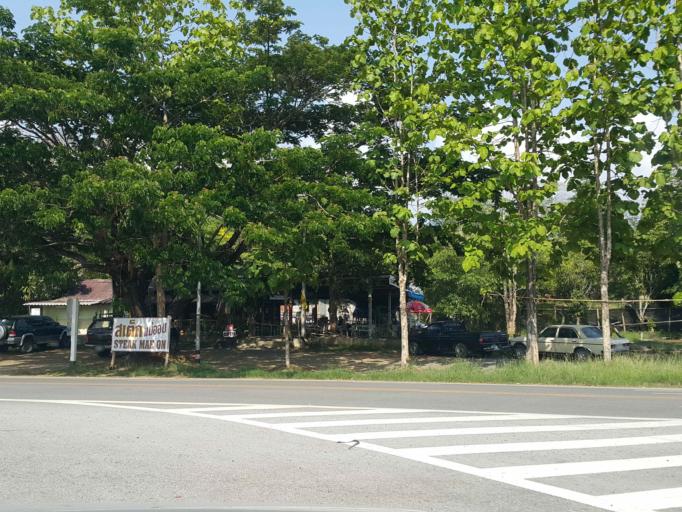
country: TH
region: Chiang Mai
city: Mae On
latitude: 18.7974
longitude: 99.2445
